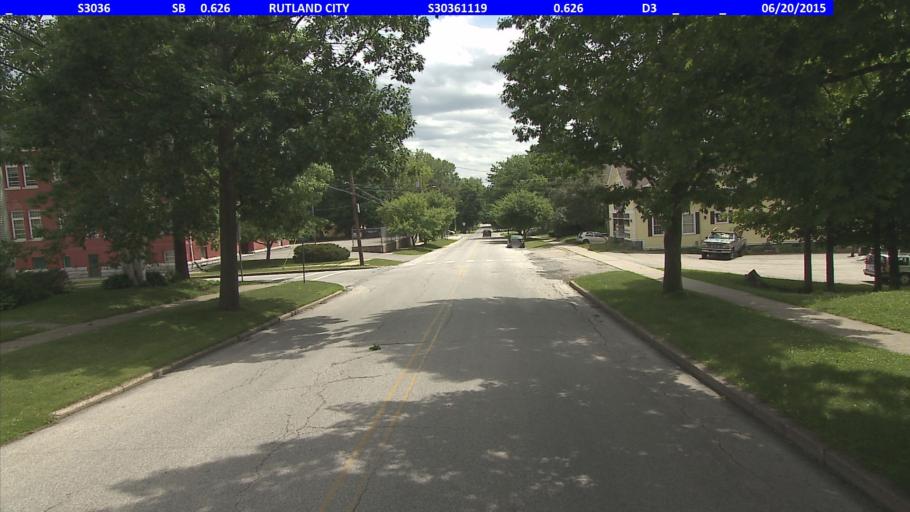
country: US
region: Vermont
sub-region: Rutland County
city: Rutland
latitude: 43.6173
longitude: -72.9773
